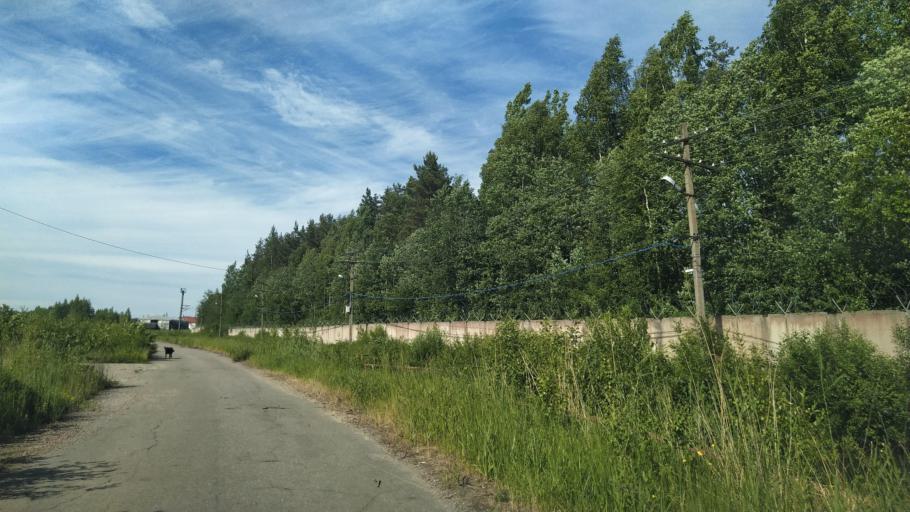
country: RU
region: Leningrad
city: Koltushi
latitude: 59.8679
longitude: 30.6695
